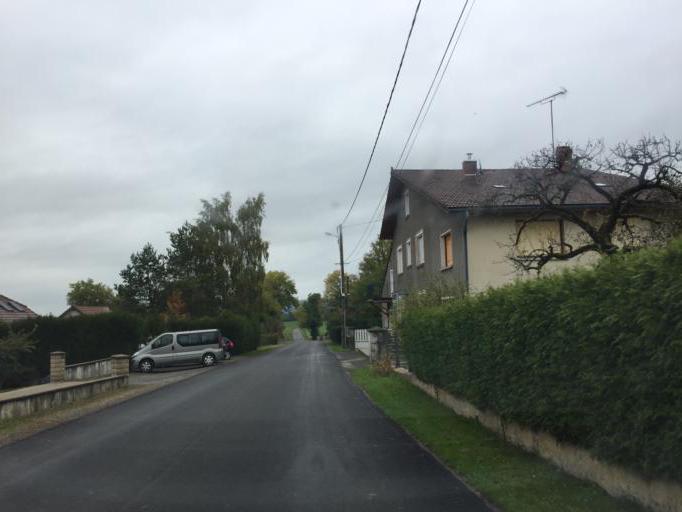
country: FR
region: Franche-Comte
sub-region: Departement du Jura
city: Orgelet
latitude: 46.5092
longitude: 5.5675
